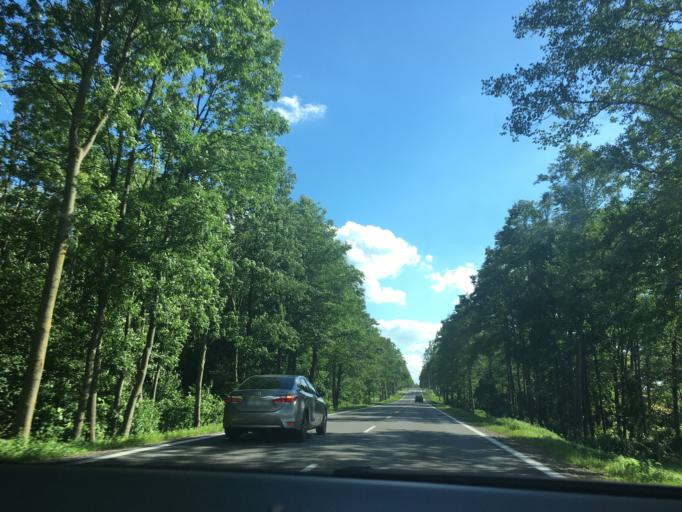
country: PL
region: Podlasie
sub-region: Powiat sokolski
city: Janow
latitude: 53.3801
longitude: 23.1108
